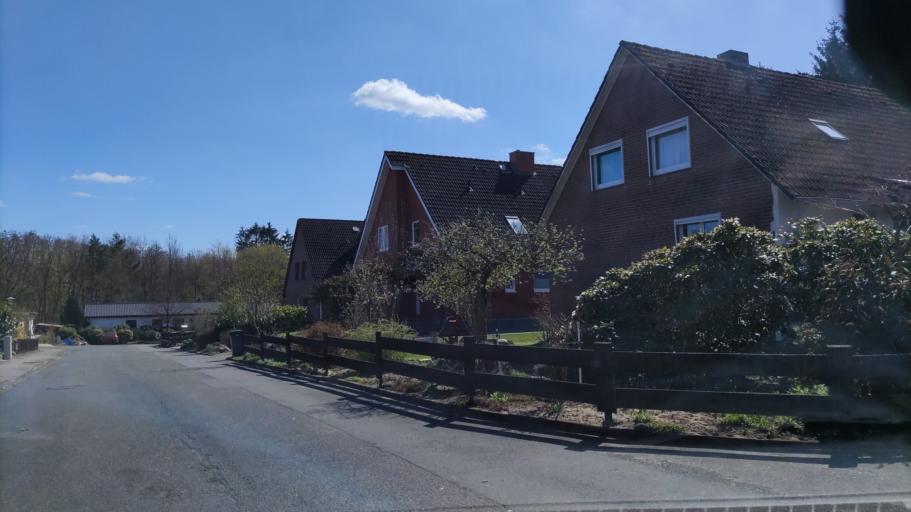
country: DE
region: Lower Saxony
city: Deutsch Evern
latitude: 53.1945
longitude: 10.4264
